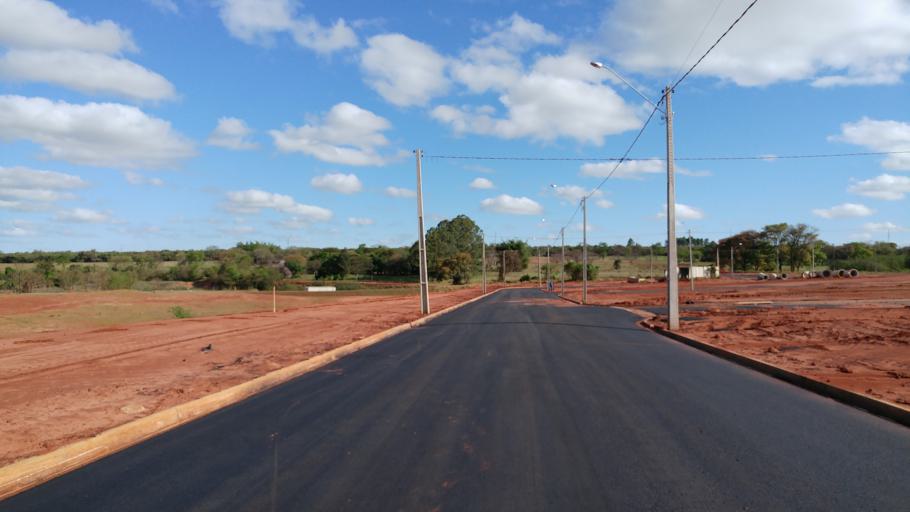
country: BR
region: Sao Paulo
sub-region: Paraguacu Paulista
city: Paraguacu Paulista
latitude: -22.4382
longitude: -50.5753
